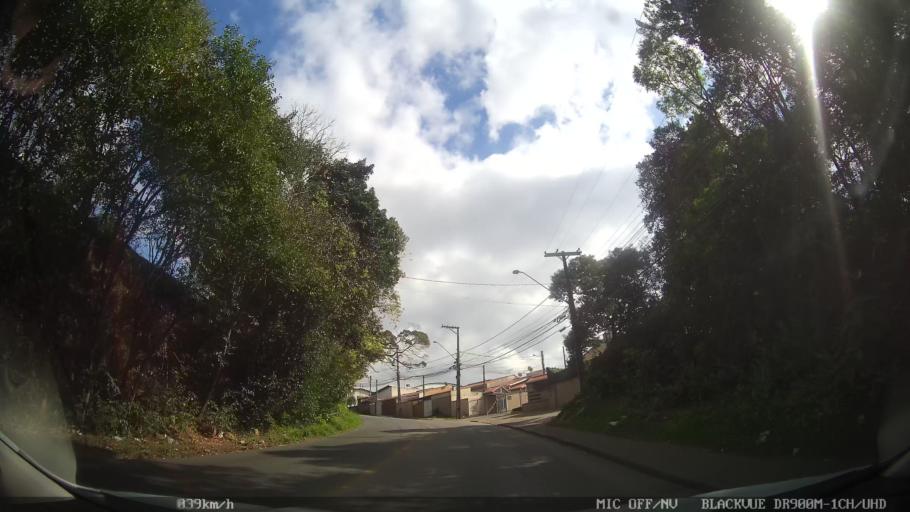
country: BR
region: Parana
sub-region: Colombo
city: Colombo
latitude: -25.3638
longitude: -49.2121
